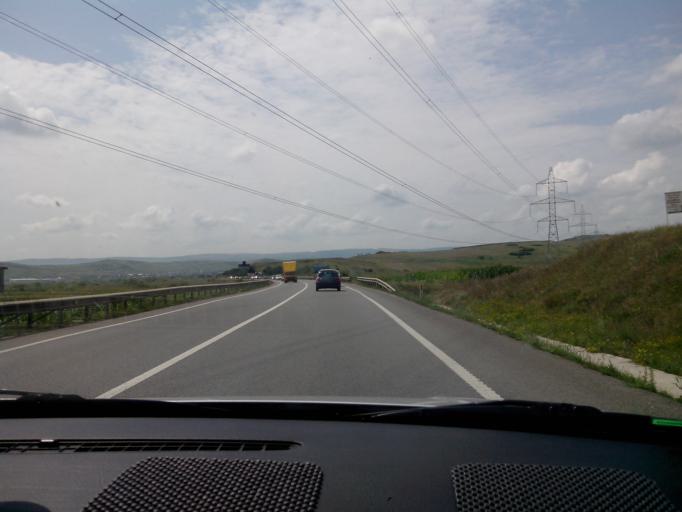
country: RO
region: Cluj
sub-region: Comuna Apahida
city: Apahida
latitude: 46.8155
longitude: 23.7384
